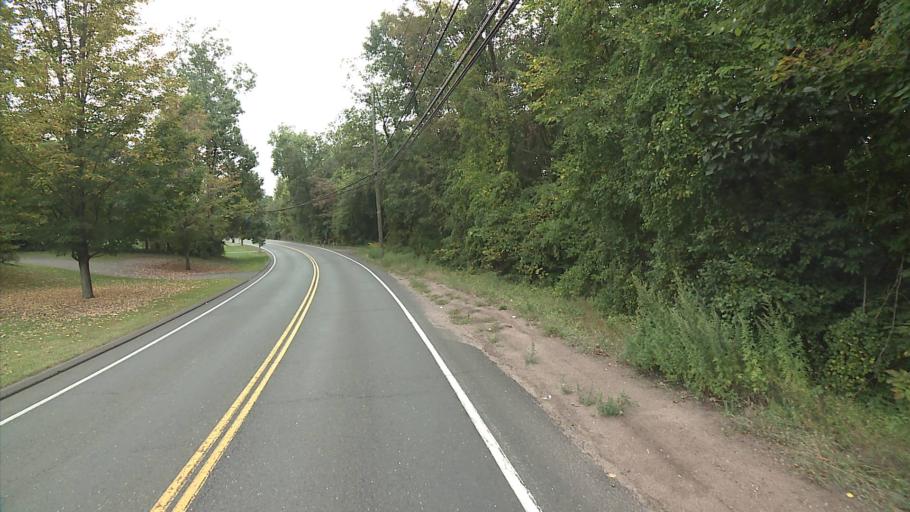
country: US
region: Connecticut
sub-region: Hartford County
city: Tariffville
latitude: 41.9054
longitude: -72.7729
